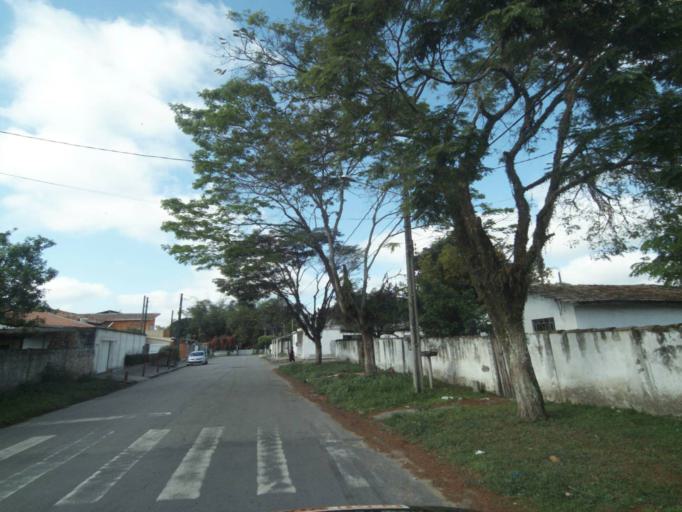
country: BR
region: Parana
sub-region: Paranagua
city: Paranagua
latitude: -25.5482
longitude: -48.5413
